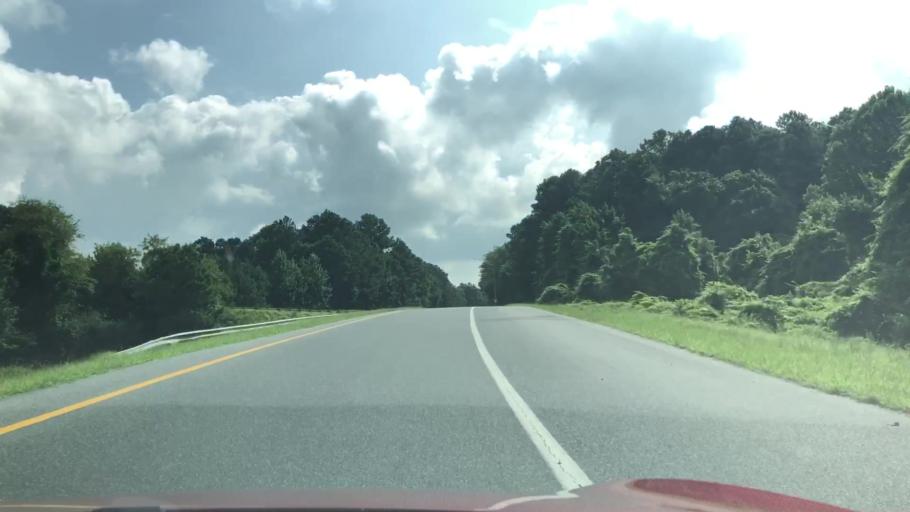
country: US
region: Maryland
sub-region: Wicomico County
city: Salisbury
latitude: 38.3949
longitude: -75.5722
